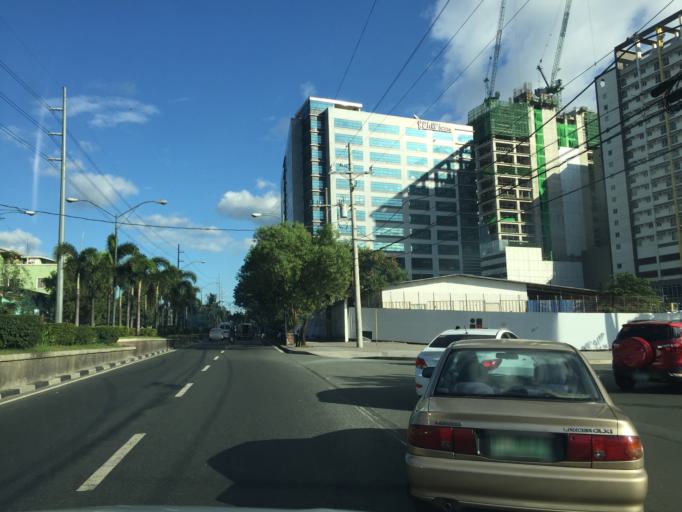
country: PH
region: Metro Manila
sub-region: Makati City
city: Makati City
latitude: 14.5616
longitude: 121.0550
